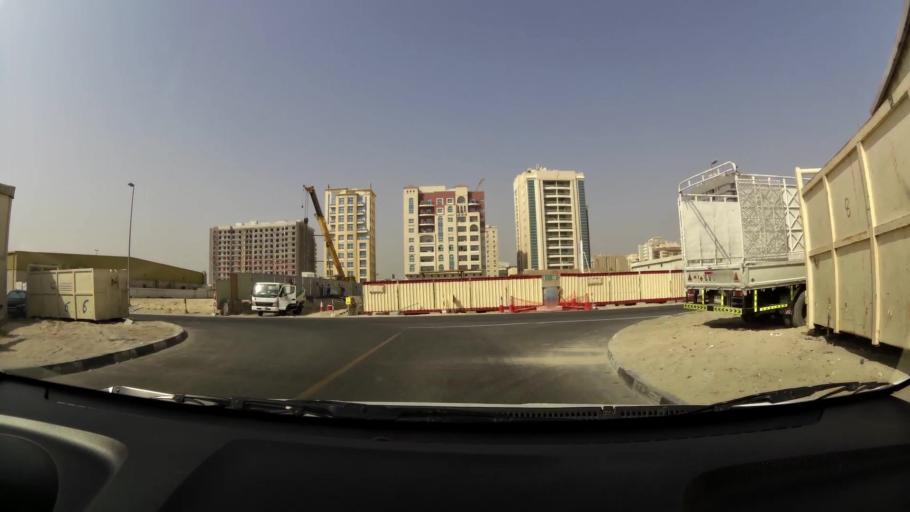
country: AE
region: Ash Shariqah
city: Sharjah
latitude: 25.2975
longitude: 55.3874
